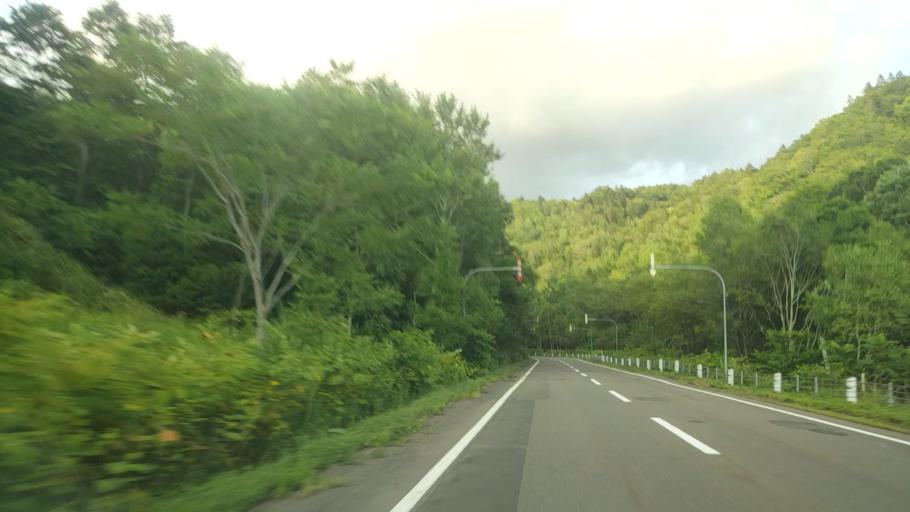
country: JP
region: Hokkaido
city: Bibai
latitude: 43.1205
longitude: 142.1018
